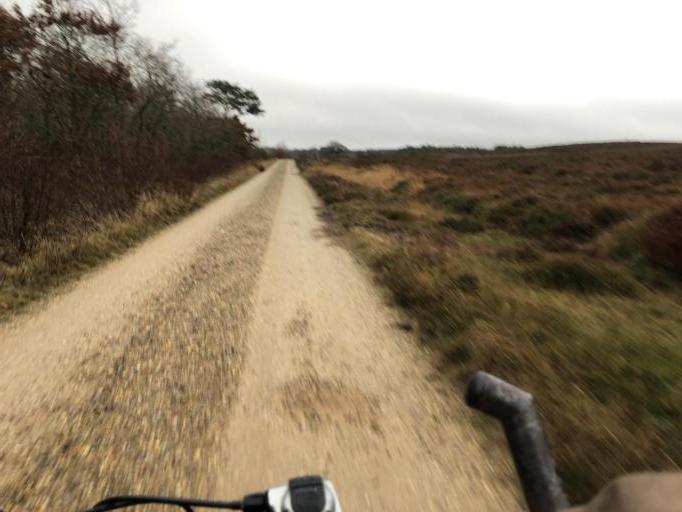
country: DK
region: Central Jutland
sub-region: Holstebro Kommune
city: Ulfborg
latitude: 56.2857
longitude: 8.4613
